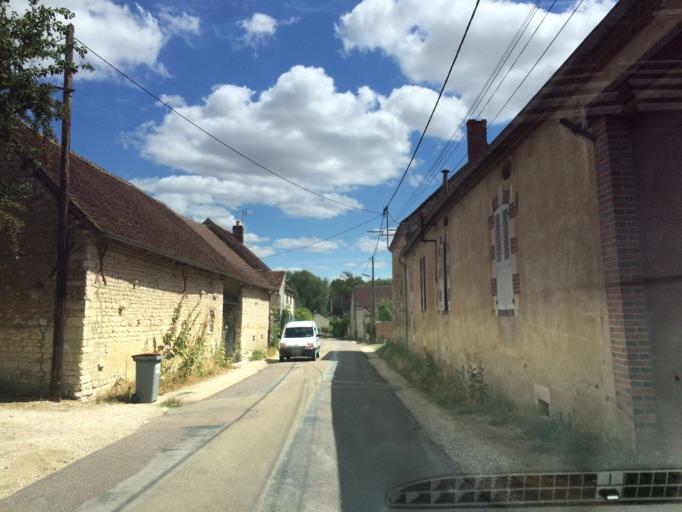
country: FR
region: Bourgogne
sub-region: Departement de l'Yonne
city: Aillant-sur-Tholon
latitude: 47.8703
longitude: 3.3987
